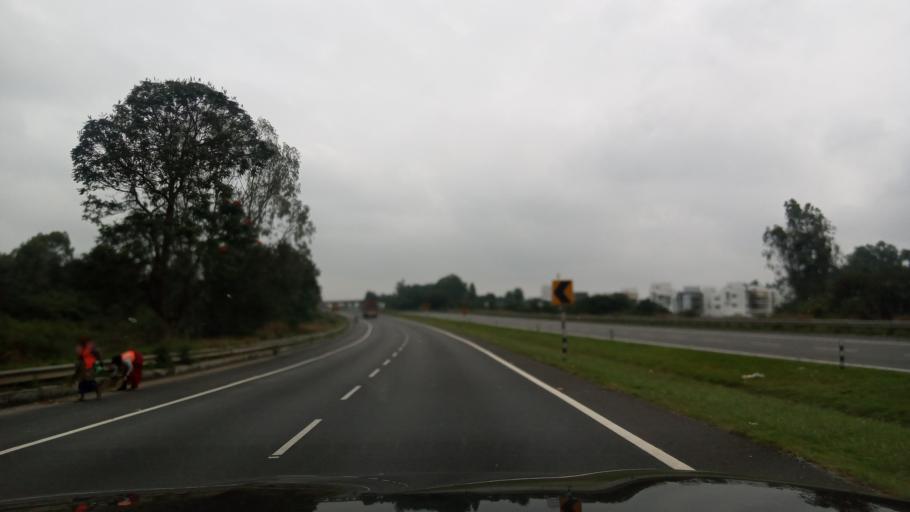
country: IN
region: Karnataka
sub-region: Bangalore Urban
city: Bangalore
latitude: 12.8538
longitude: 77.6038
